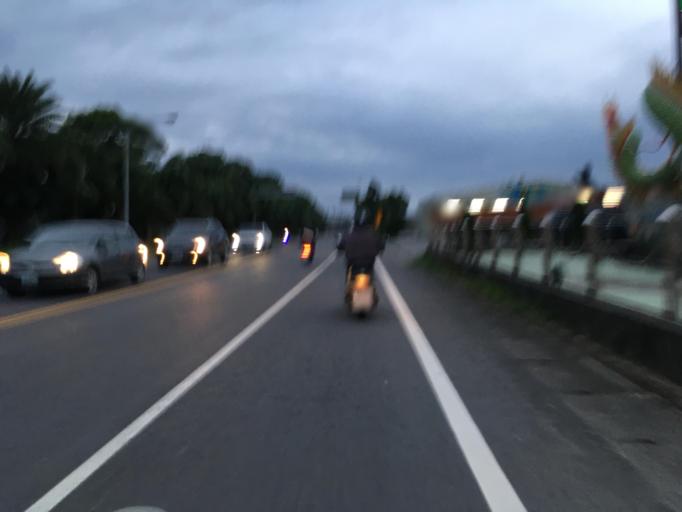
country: TW
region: Taiwan
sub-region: Yilan
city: Yilan
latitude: 24.6352
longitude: 121.8320
